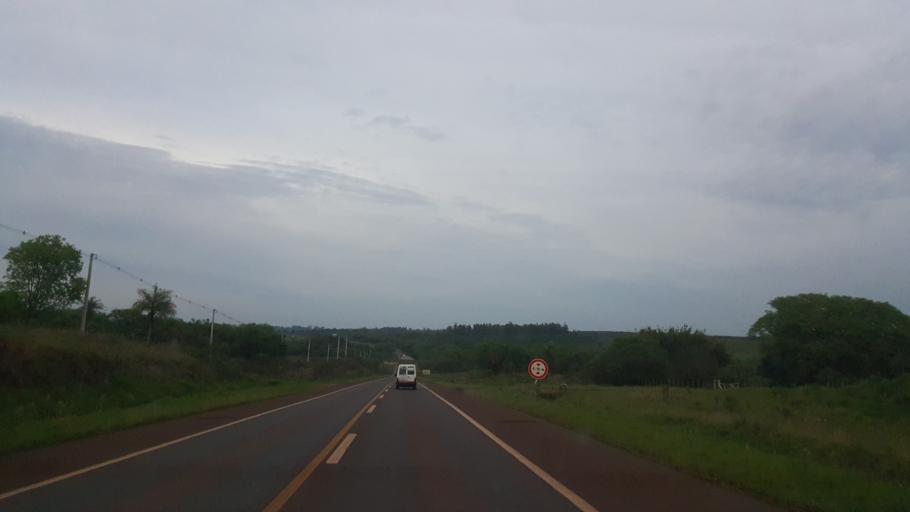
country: AR
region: Misiones
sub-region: Departamento de Apostoles
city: San Jose
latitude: -27.7616
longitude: -55.7927
